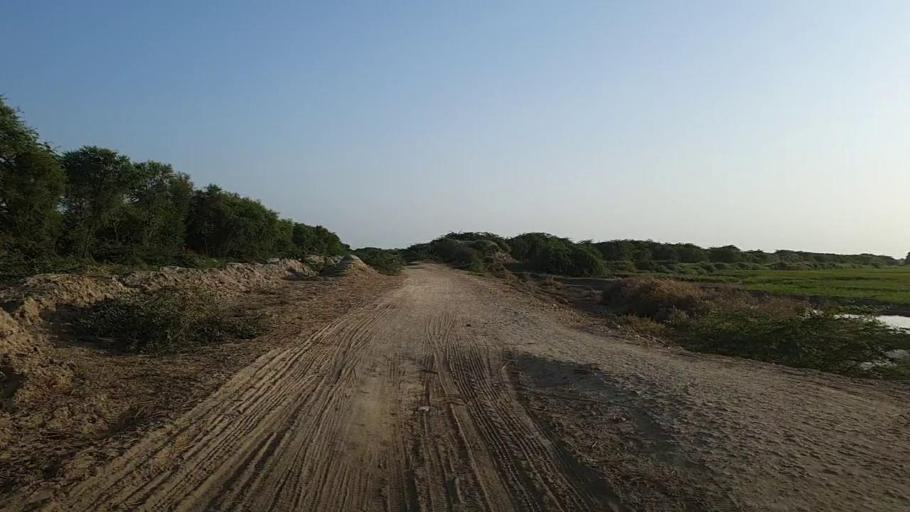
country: PK
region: Sindh
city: Kario
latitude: 24.7122
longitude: 68.6669
